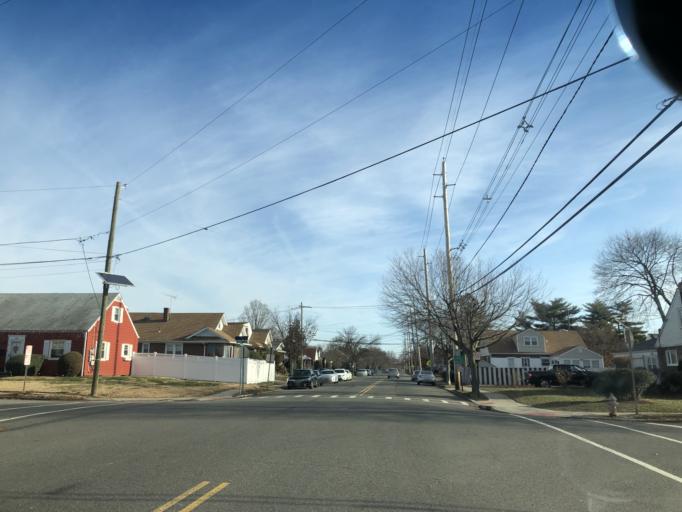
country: US
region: New Jersey
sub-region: Bergen County
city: Fair Lawn
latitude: 40.9322
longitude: -74.1274
